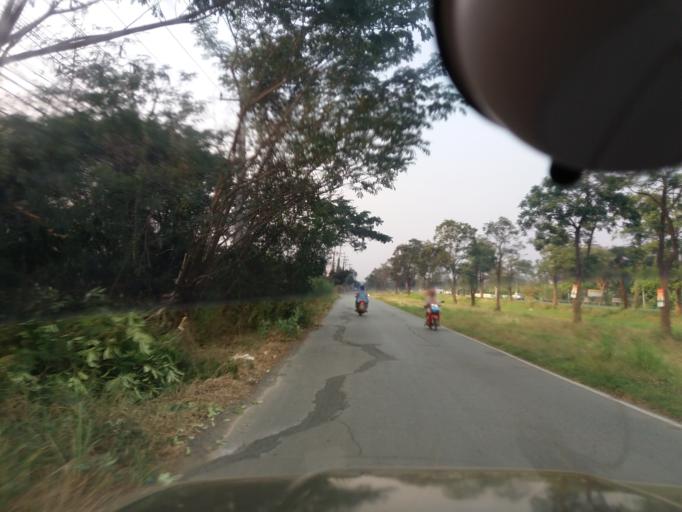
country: TH
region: Sing Buri
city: Sing Buri
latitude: 14.8833
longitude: 100.4014
